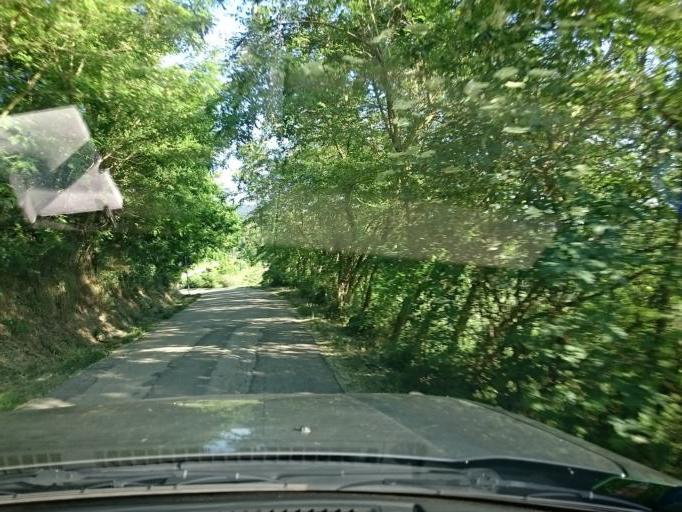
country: IT
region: Veneto
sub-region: Provincia di Padova
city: Galzignano
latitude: 45.2974
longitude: 11.7054
